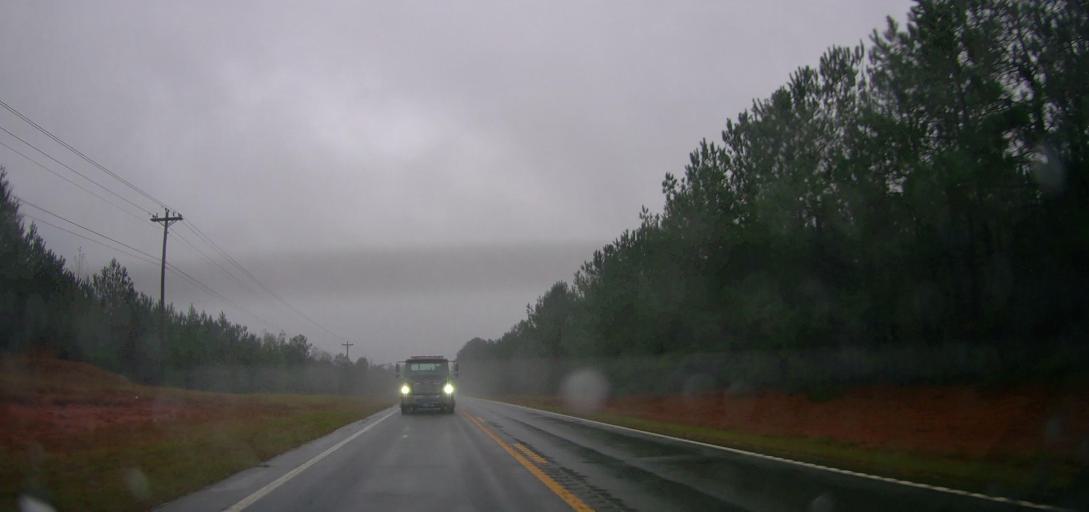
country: US
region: Georgia
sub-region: Jones County
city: Gray
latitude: 33.0933
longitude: -83.4854
